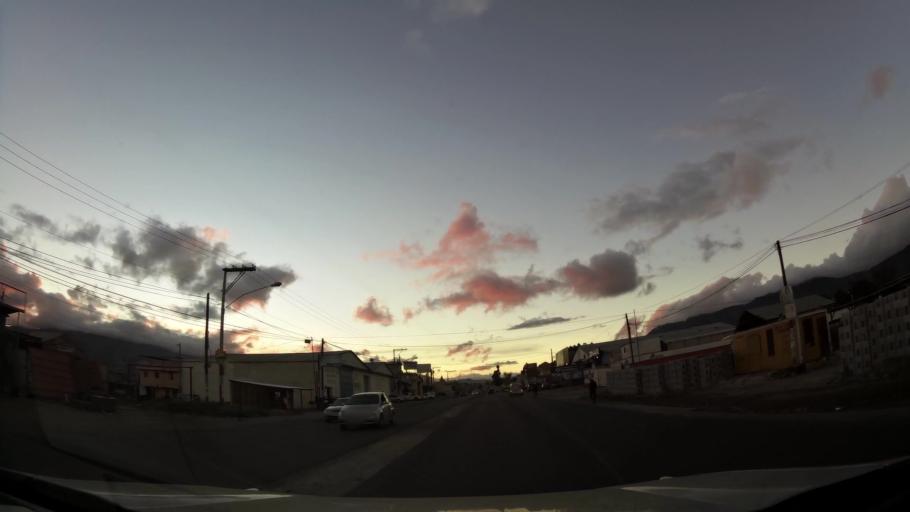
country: GT
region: Quetzaltenango
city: Olintepeque
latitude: 14.8624
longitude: -91.5295
